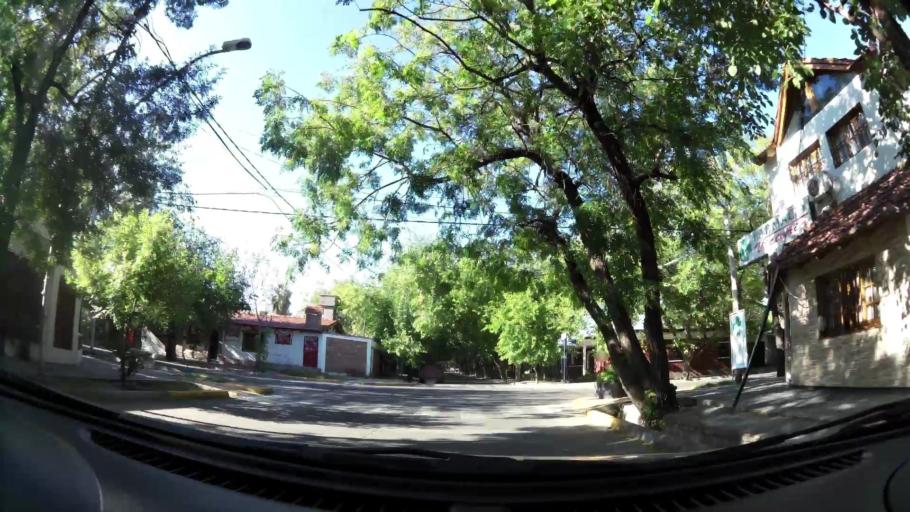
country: AR
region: Mendoza
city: Las Heras
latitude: -32.8661
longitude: -68.8476
